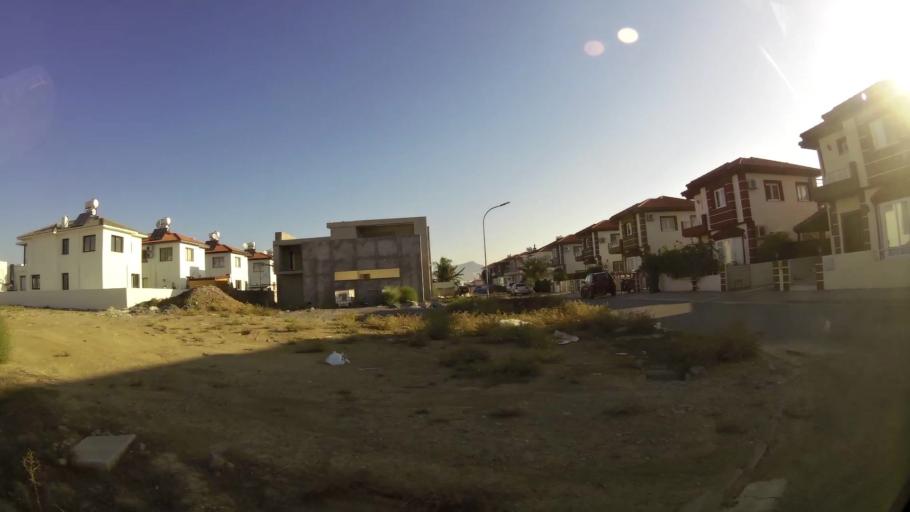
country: CY
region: Lefkosia
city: Nicosia
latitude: 35.2026
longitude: 33.2939
